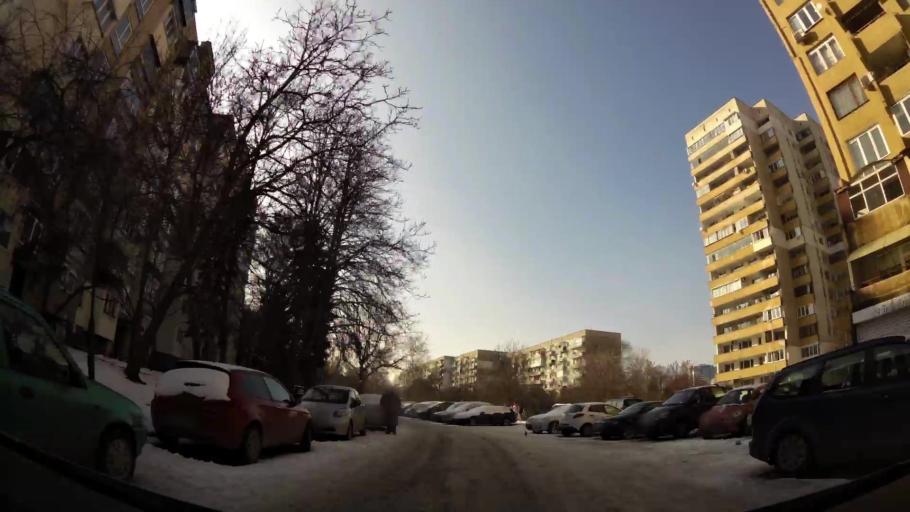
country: BG
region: Sofia-Capital
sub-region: Stolichna Obshtina
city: Sofia
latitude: 42.6644
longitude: 23.3535
